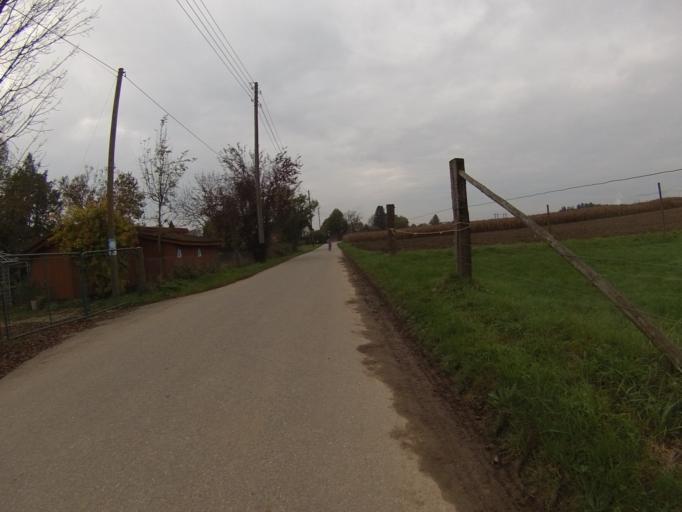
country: CH
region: Geneva
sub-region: Geneva
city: Meyrin
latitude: 46.2374
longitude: 6.0670
